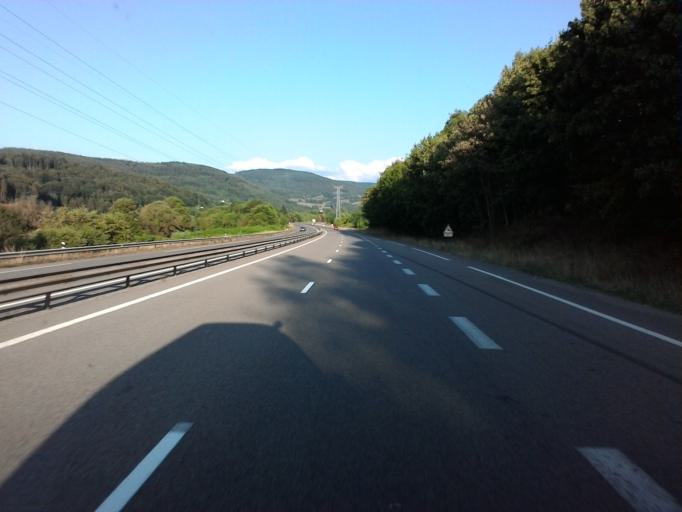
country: FR
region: Lorraine
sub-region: Departement des Vosges
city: Pouxeux
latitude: 48.1085
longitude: 6.5785
